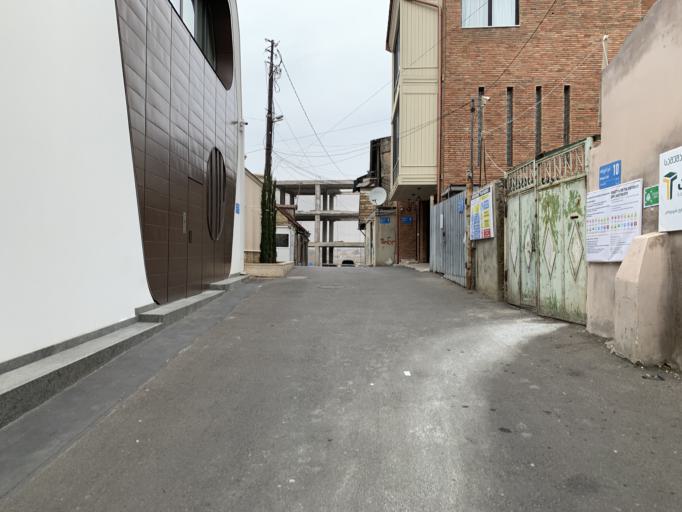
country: GE
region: T'bilisi
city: Tbilisi
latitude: 41.6963
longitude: 44.8106
